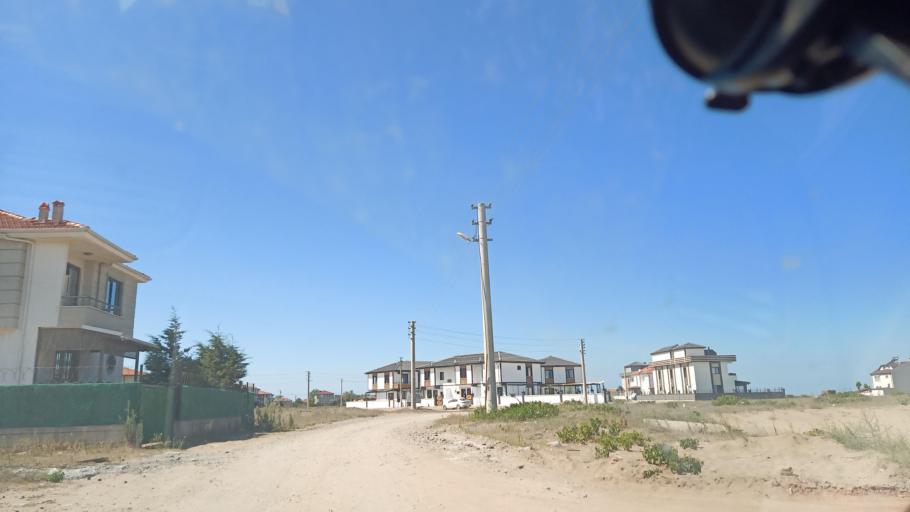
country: TR
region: Sakarya
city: Karasu
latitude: 41.1229
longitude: 30.6558
